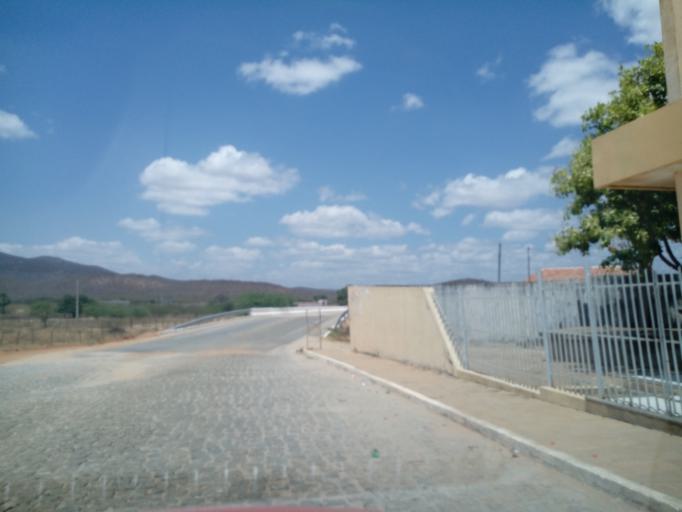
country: BR
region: Paraiba
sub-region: Patos
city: Patos
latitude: -7.0328
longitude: -37.1479
